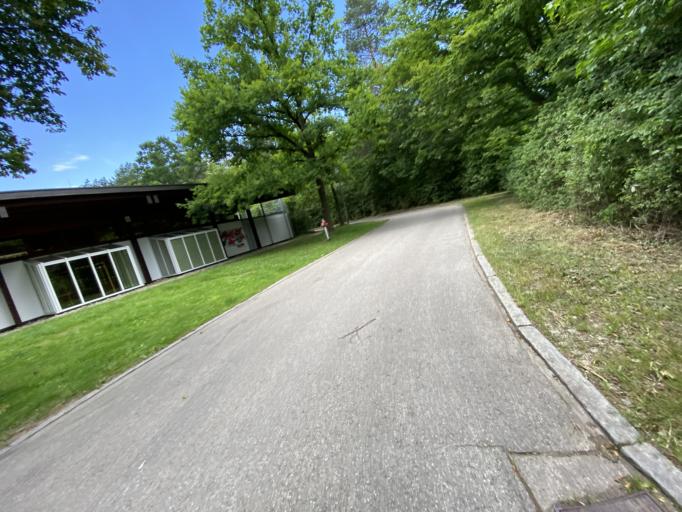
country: DE
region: Bavaria
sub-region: Upper Bavaria
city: Grafelfing
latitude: 48.1265
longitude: 11.4323
